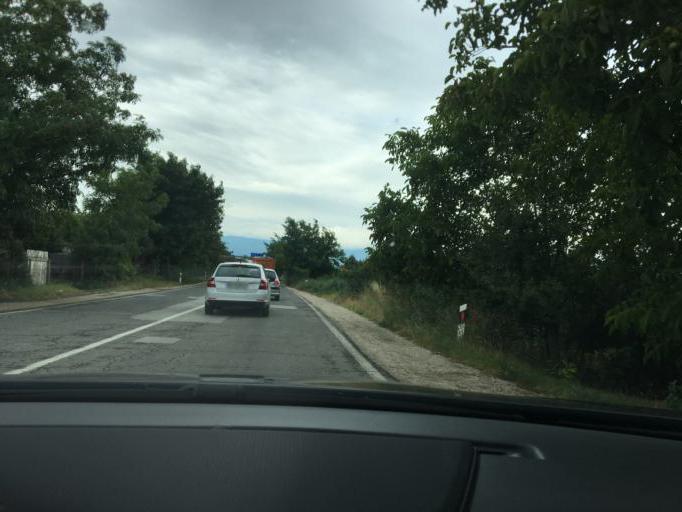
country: MK
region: Kumanovo
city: Kumanovo
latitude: 42.1619
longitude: 21.7360
